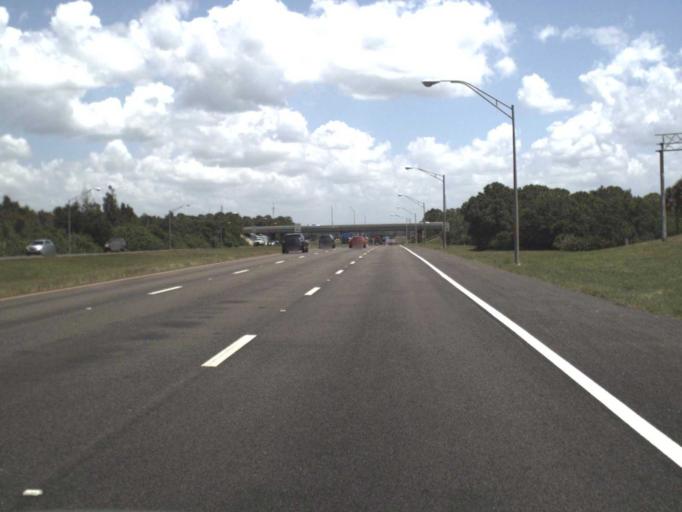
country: US
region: Florida
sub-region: Pinellas County
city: Lealman
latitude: 27.8506
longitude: -82.6675
